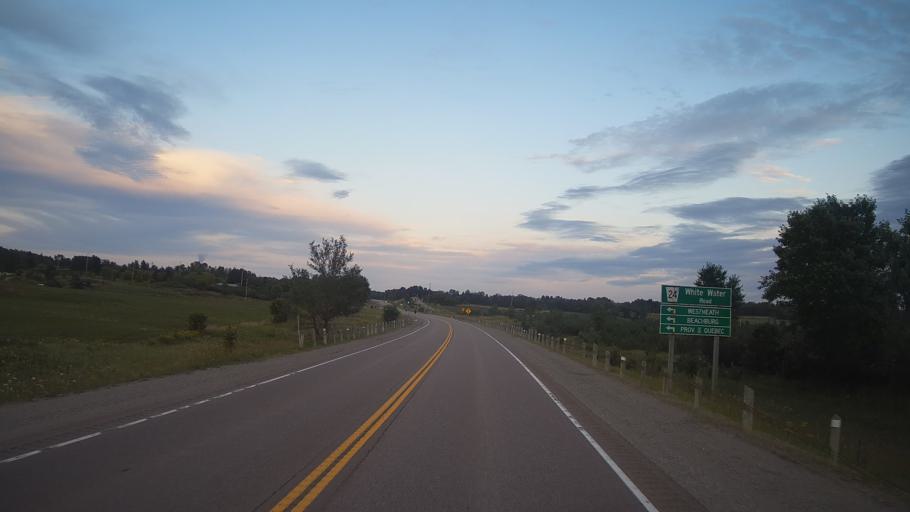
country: CA
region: Ontario
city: Pembroke
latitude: 45.7652
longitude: -77.0741
